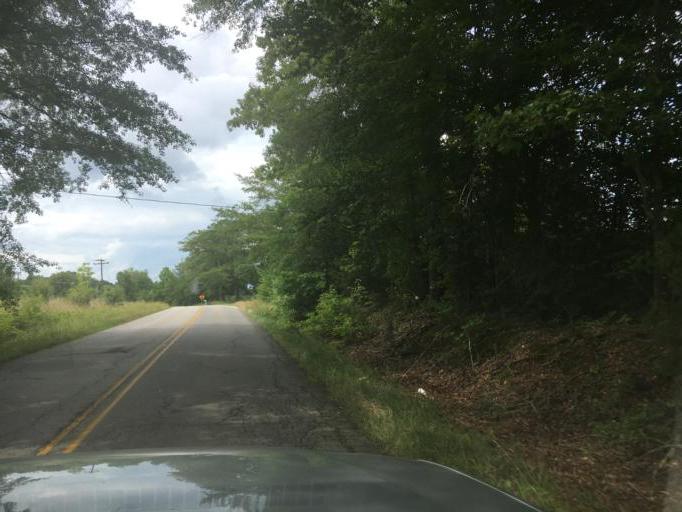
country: US
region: South Carolina
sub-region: Laurens County
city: Watts Mills
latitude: 34.5297
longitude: -81.9661
